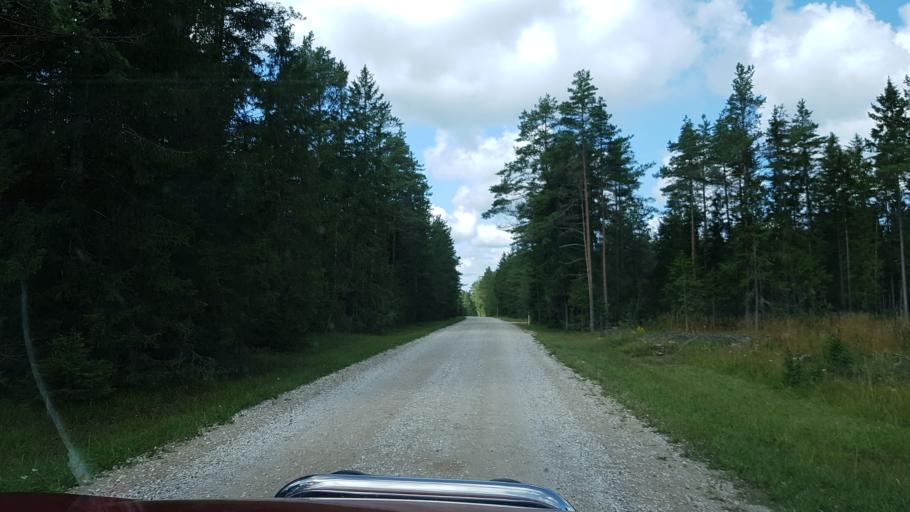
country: EE
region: Raplamaa
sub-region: Rapla vald
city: Rapla
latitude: 58.9556
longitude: 24.6600
